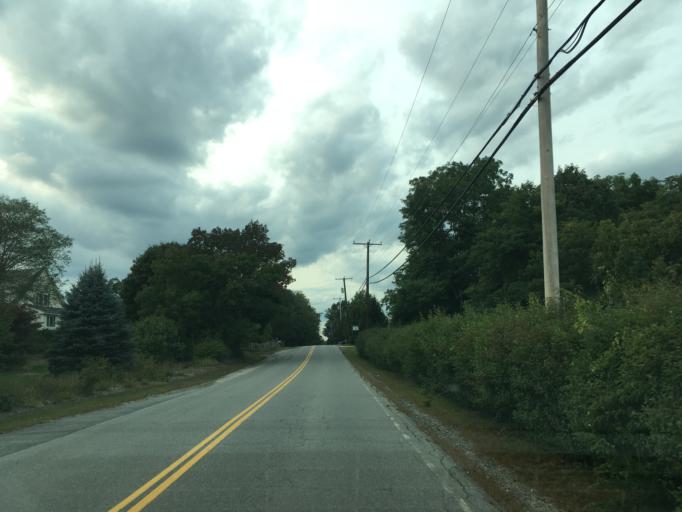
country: US
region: New Hampshire
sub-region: Rockingham County
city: Stratham Station
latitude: 43.0014
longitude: -70.8936
